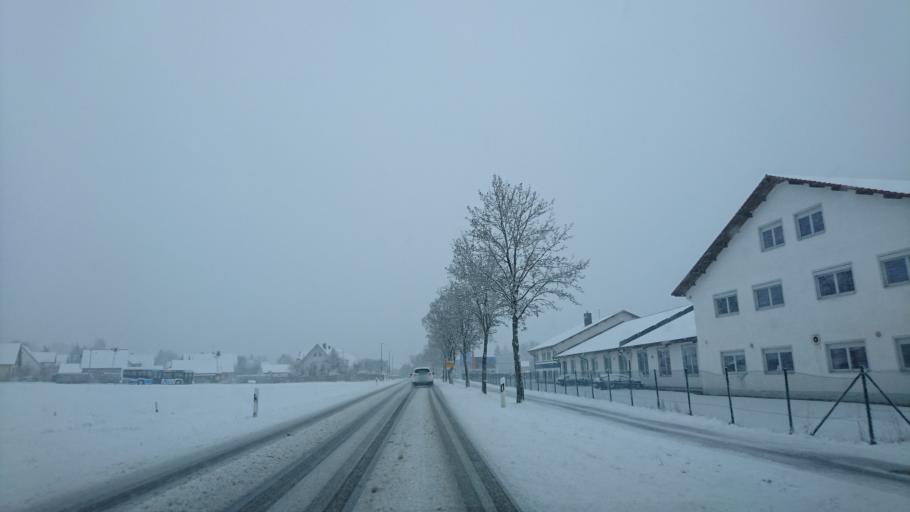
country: DE
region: Bavaria
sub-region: Swabia
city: Emersacker
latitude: 48.4966
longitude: 10.6772
